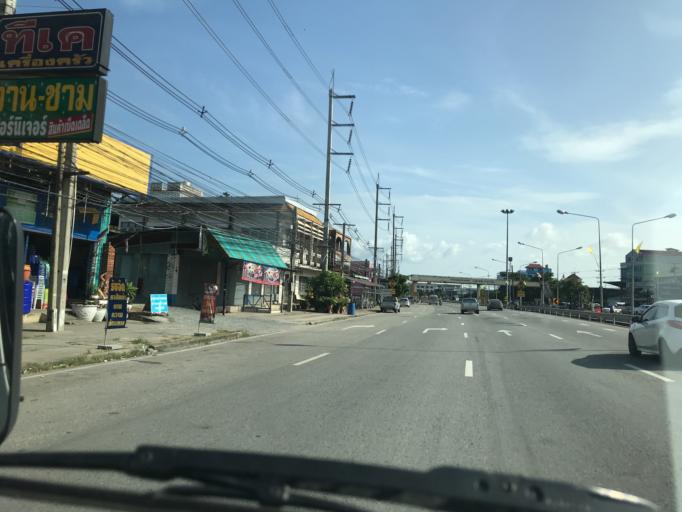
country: TH
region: Chon Buri
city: Bang Lamung
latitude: 13.0178
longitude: 100.9317
